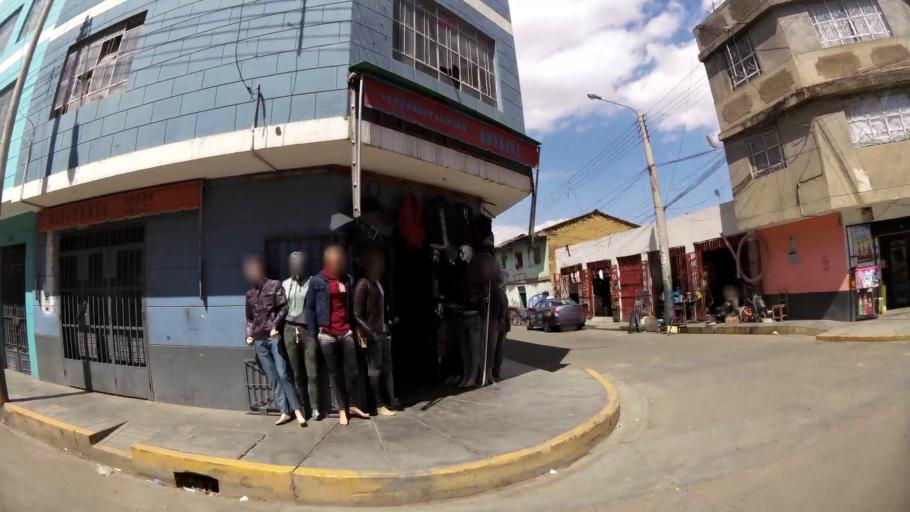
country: PE
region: Junin
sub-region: Provincia de Huancayo
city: Huancayo
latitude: -12.0706
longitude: -75.2021
